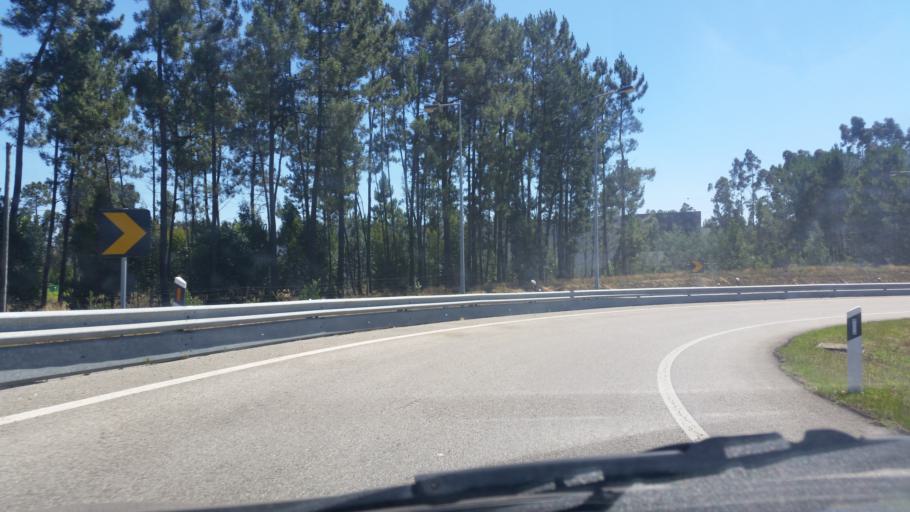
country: PT
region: Aveiro
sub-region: Agueda
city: Valongo
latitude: 40.5947
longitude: -8.4678
